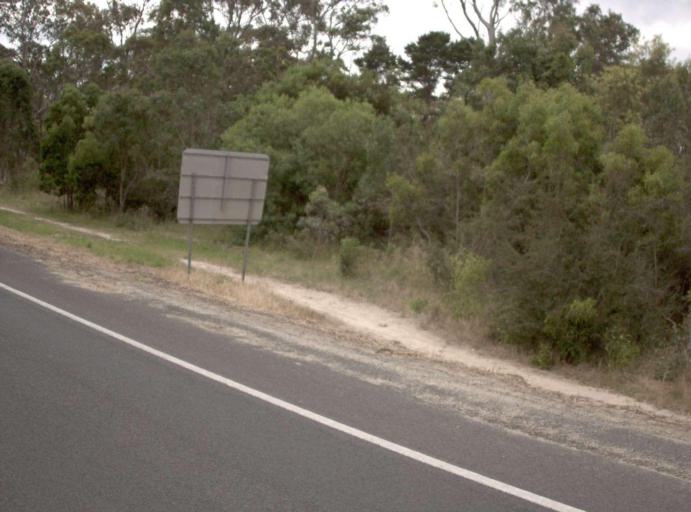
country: AU
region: Victoria
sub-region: Wellington
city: Sale
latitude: -38.1714
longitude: 147.0880
